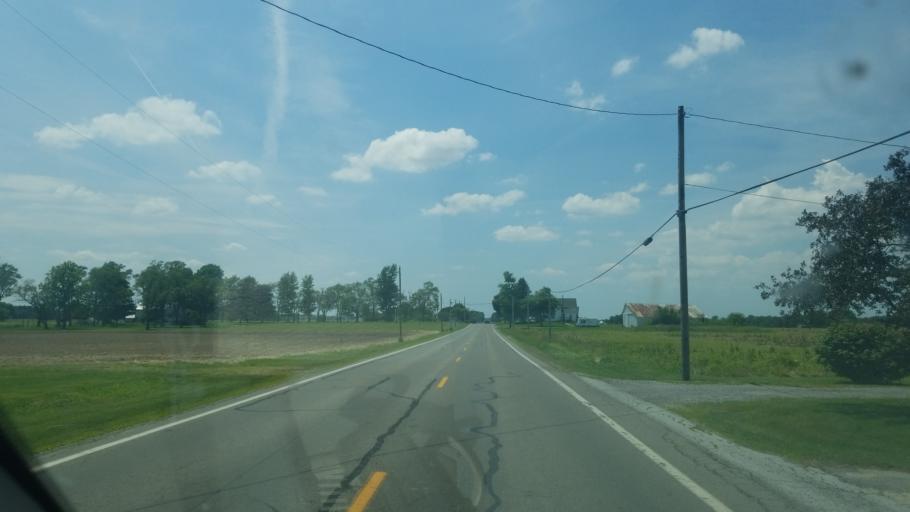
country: US
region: Ohio
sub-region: Hardin County
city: Ada
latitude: 40.7765
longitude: -83.8531
